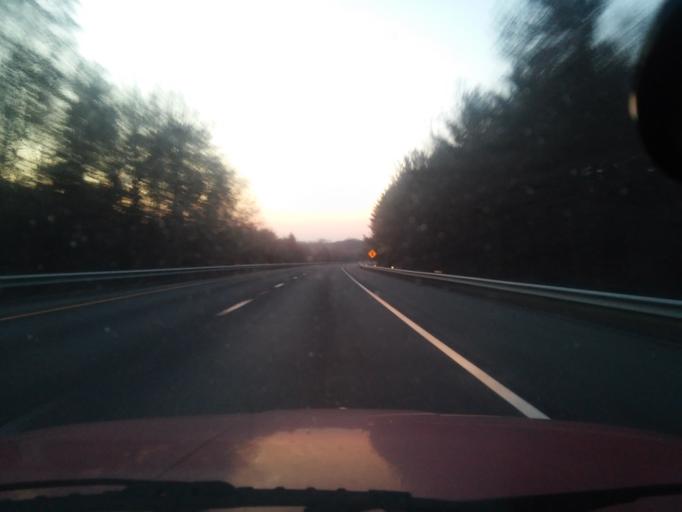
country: US
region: Virginia
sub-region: Fluvanna County
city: Lake Monticello
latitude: 37.9977
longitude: -78.3379
